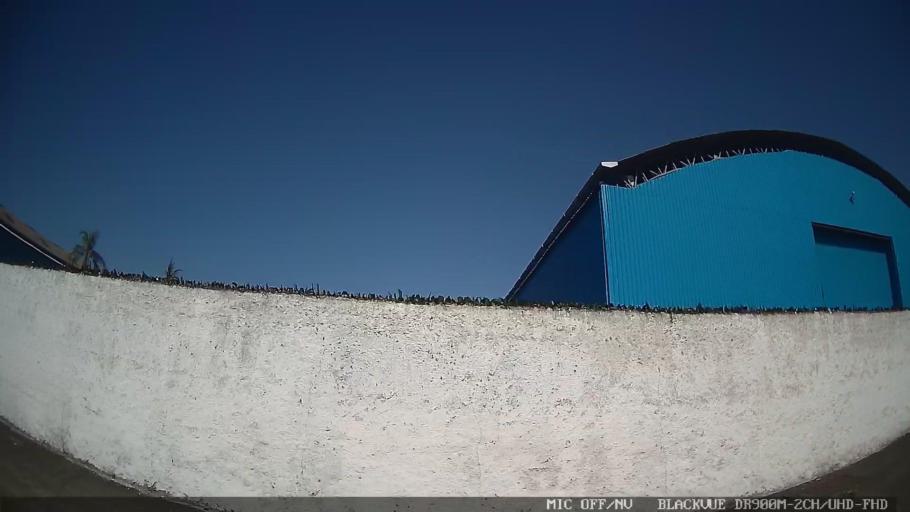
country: BR
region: Sao Paulo
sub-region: Guaruja
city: Guaruja
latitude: -24.0013
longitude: -46.2911
